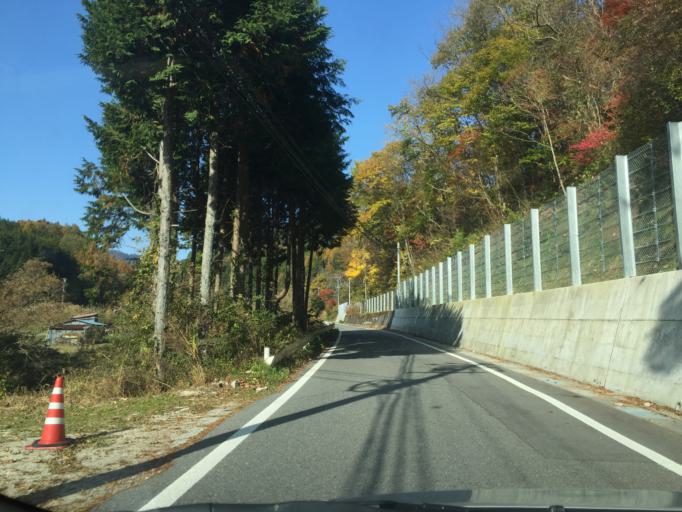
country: JP
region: Nagano
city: Iida
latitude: 35.3795
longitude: 137.6867
